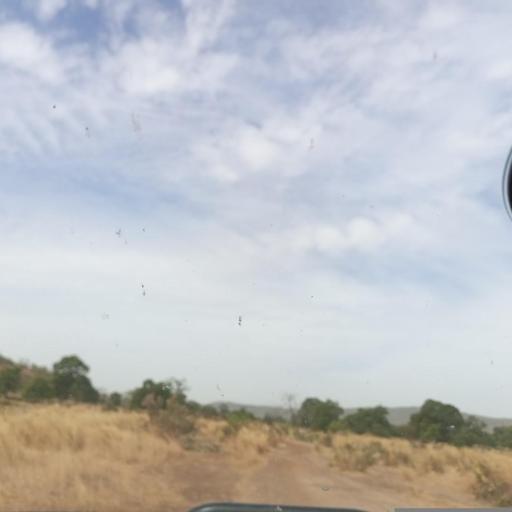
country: ML
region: Koulikoro
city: Koulikoro
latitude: 13.1742
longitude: -7.7386
